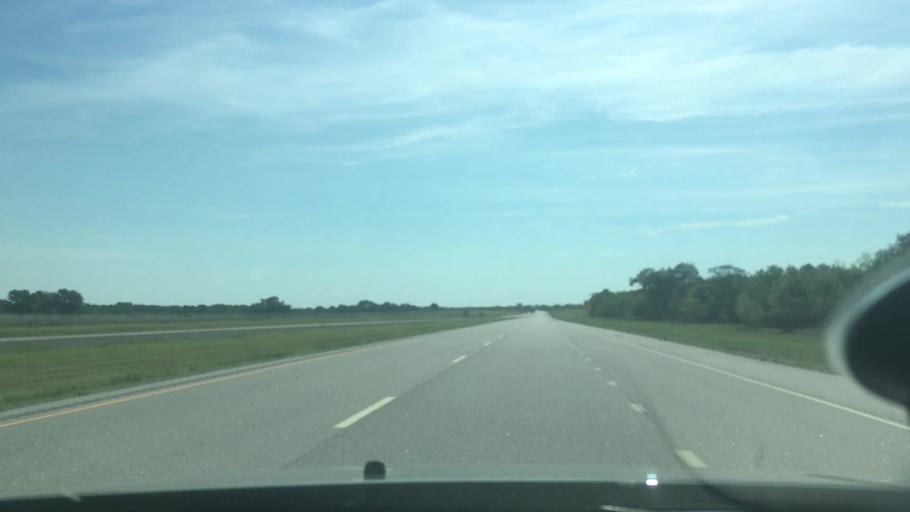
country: US
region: Oklahoma
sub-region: Bryan County
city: Durant
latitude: 33.9653
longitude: -96.3663
